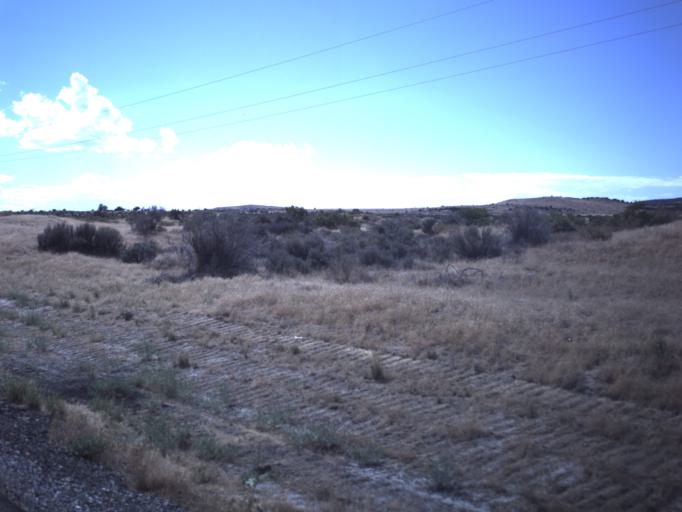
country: US
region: Utah
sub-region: Tooele County
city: Grantsville
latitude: 40.2394
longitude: -112.7153
